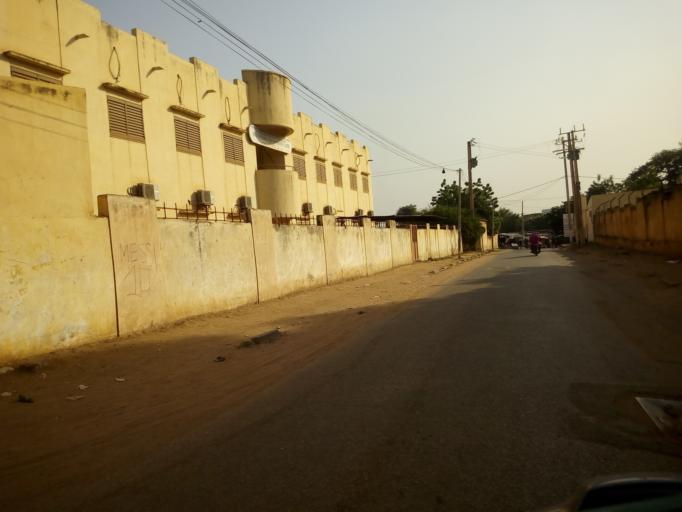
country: ML
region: Kayes
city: Kayes
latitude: 14.4482
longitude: -11.4328
